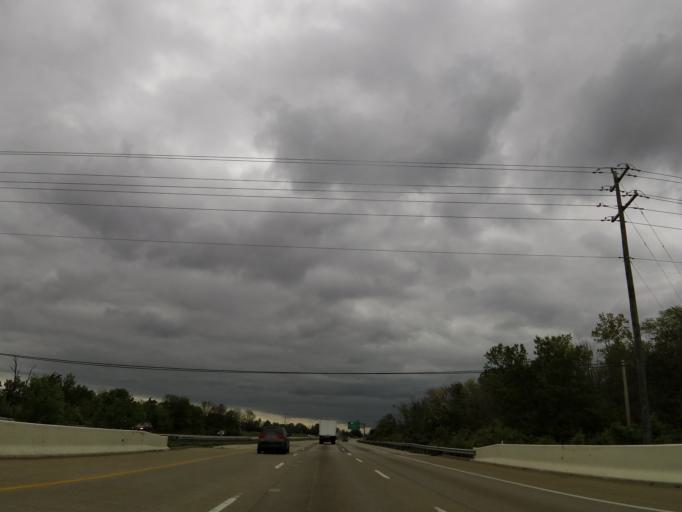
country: US
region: Ohio
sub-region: Warren County
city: Landen
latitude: 39.3363
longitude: -84.2821
